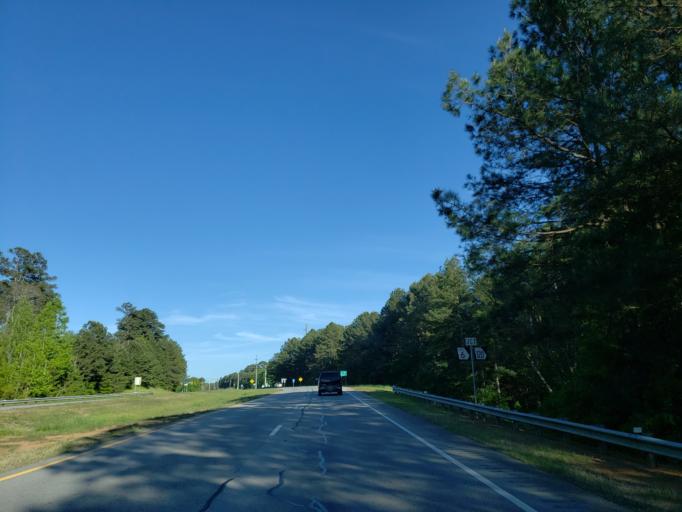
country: US
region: Georgia
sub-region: Paulding County
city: Dallas
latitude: 33.9161
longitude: -84.8604
